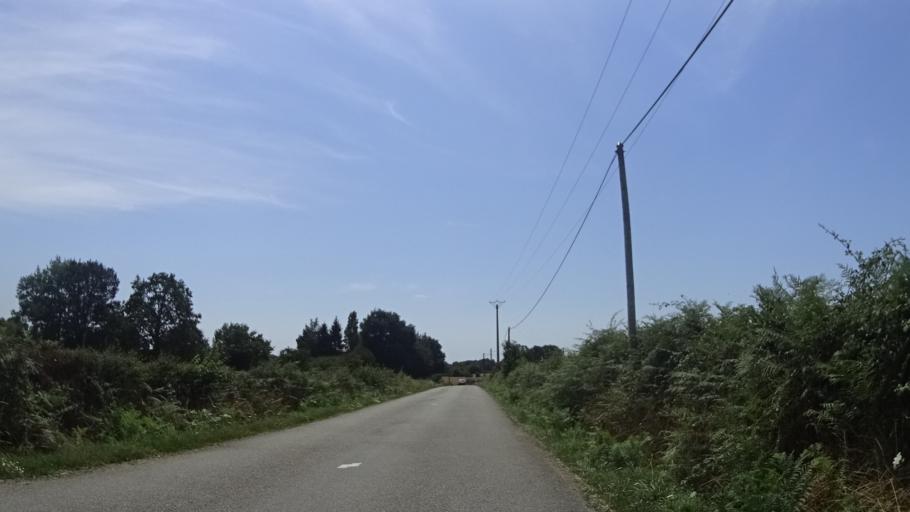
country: FR
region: Pays de la Loire
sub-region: Departement de la Loire-Atlantique
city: Bouvron
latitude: 47.3958
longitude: -1.8244
